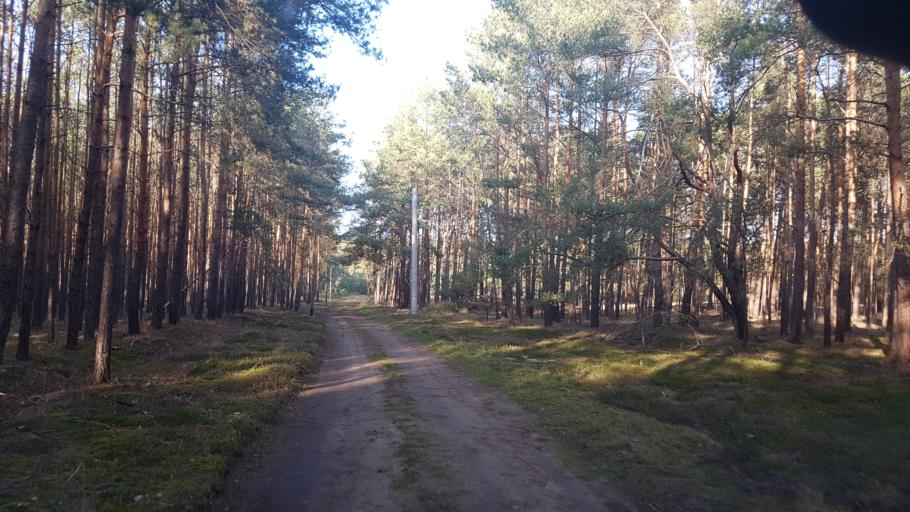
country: DE
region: Brandenburg
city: Schilda
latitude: 51.6438
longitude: 13.3489
